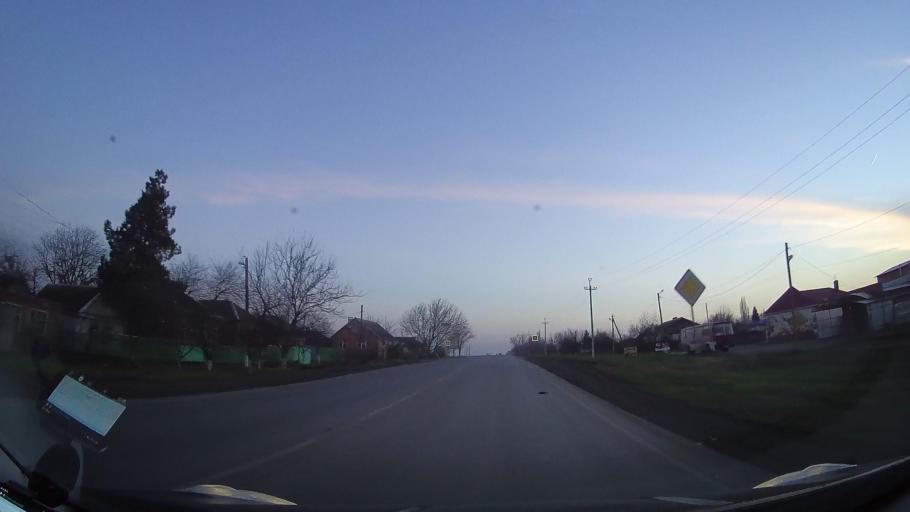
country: RU
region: Rostov
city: Zernograd
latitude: 46.8367
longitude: 40.2994
